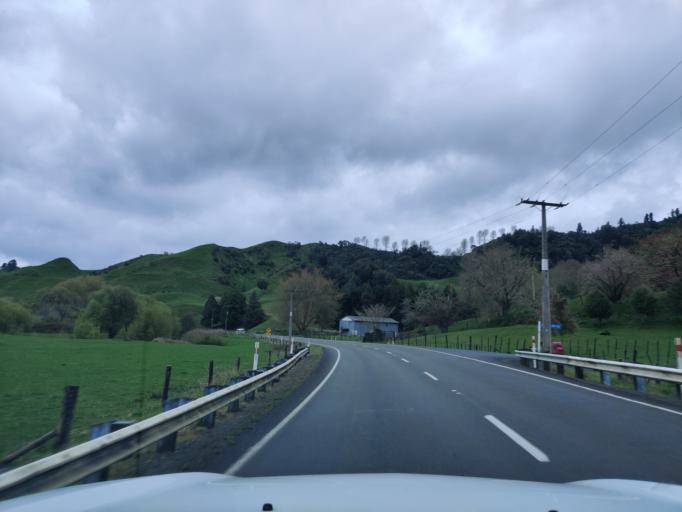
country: NZ
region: Waikato
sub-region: Otorohanga District
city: Otorohanga
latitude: -38.4879
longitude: 175.1864
